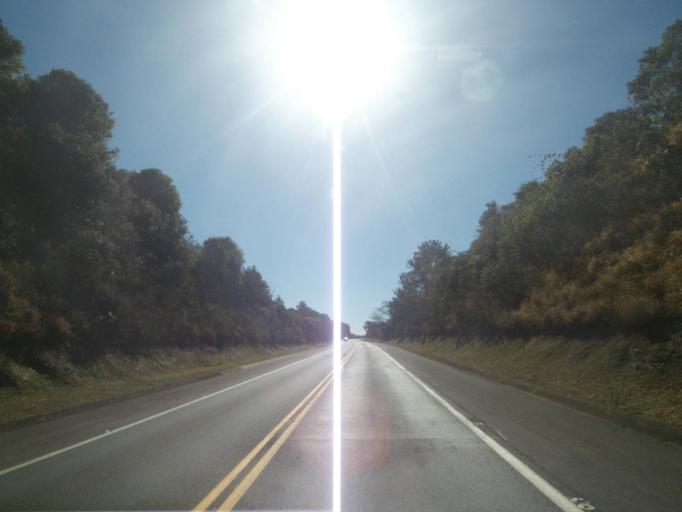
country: BR
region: Parana
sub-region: Tibagi
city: Tibagi
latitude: -24.7379
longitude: -50.5373
